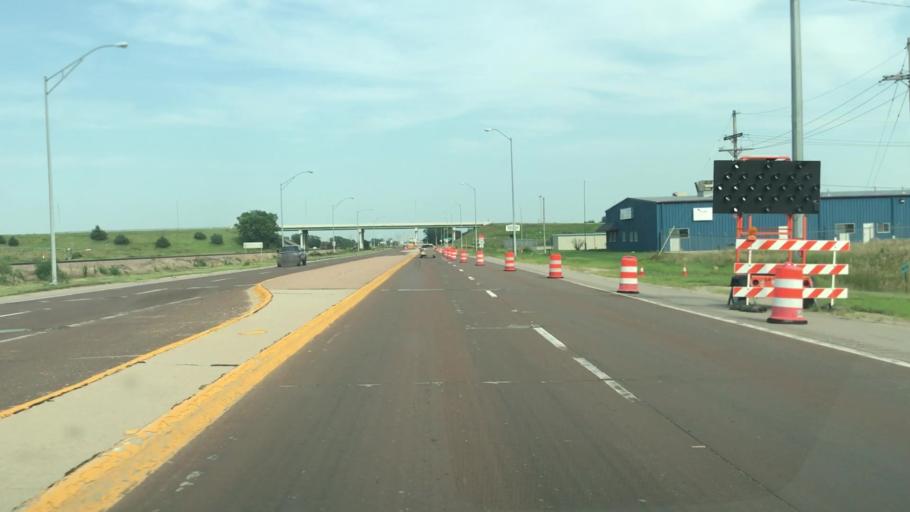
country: US
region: Nebraska
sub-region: Hall County
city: Grand Island
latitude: 40.9545
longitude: -98.3887
